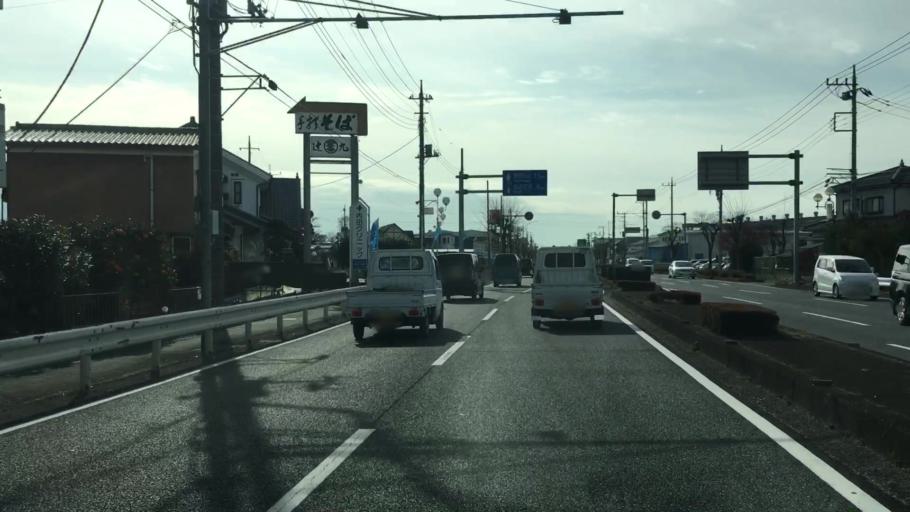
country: JP
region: Saitama
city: Menuma
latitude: 36.2274
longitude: 139.3704
